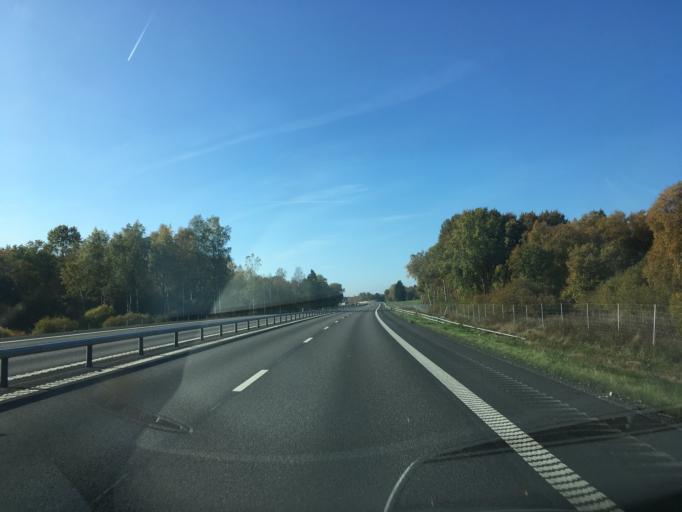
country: SE
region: Skane
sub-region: Horby Kommun
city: Hoerby
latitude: 55.9256
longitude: 13.8227
